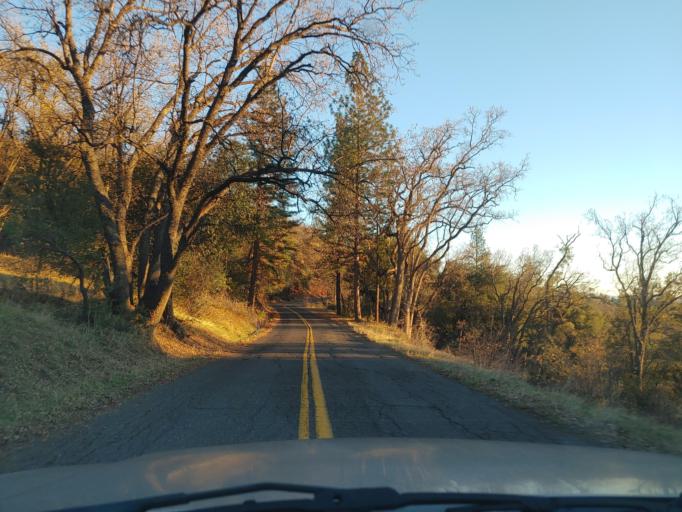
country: US
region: California
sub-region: Tuolumne County
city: Cedar Ridge
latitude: 38.0414
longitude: -120.3128
